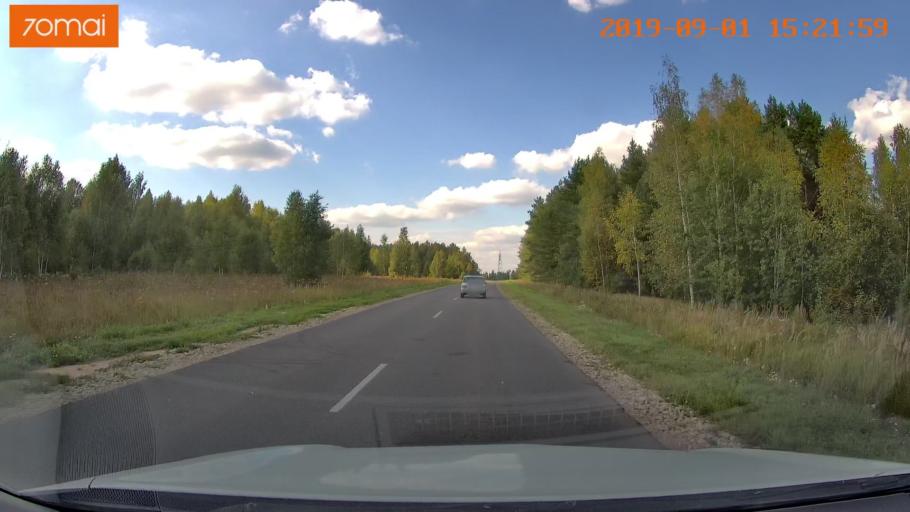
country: RU
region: Kaluga
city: Maloyaroslavets
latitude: 54.9328
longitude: 36.4688
